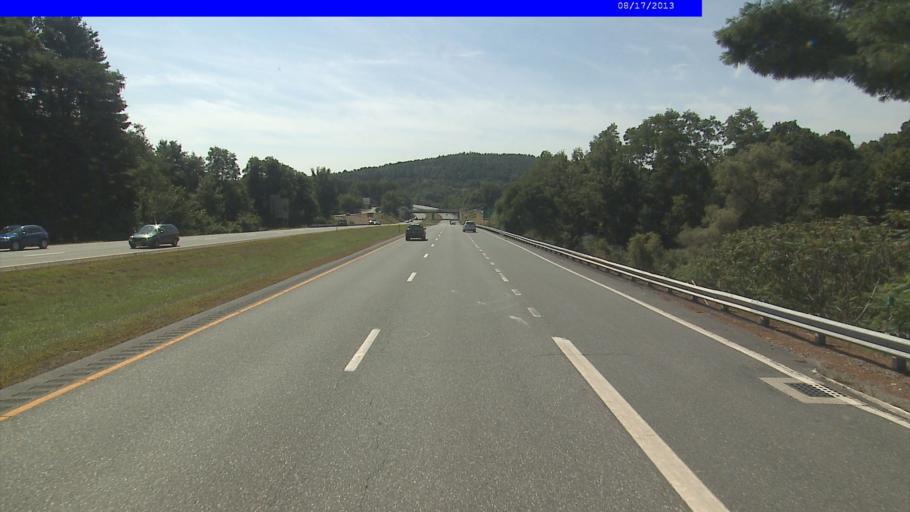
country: US
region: Vermont
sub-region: Windham County
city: West Brattleboro
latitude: 42.8546
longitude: -72.5806
